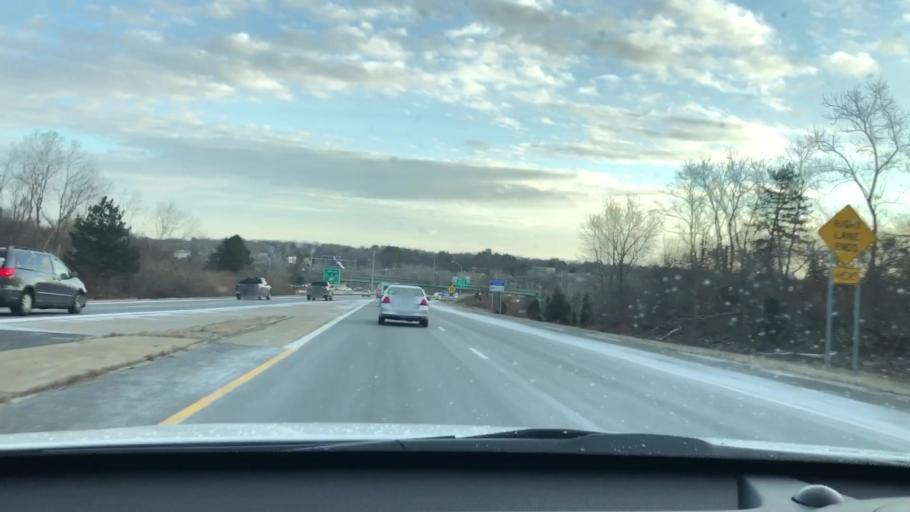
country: US
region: Massachusetts
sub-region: Norfolk County
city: Braintree
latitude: 42.2265
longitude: -71.0150
